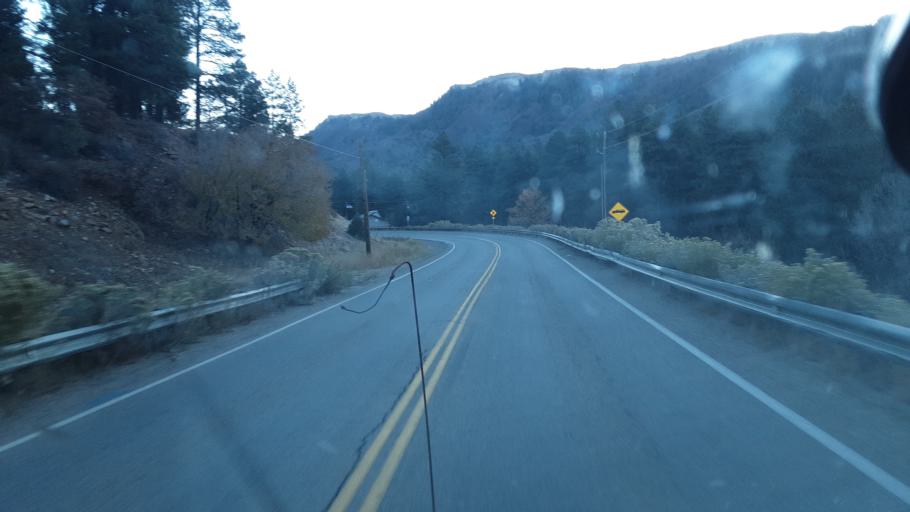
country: US
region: Colorado
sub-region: La Plata County
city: Durango
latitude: 37.3115
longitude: -107.7797
